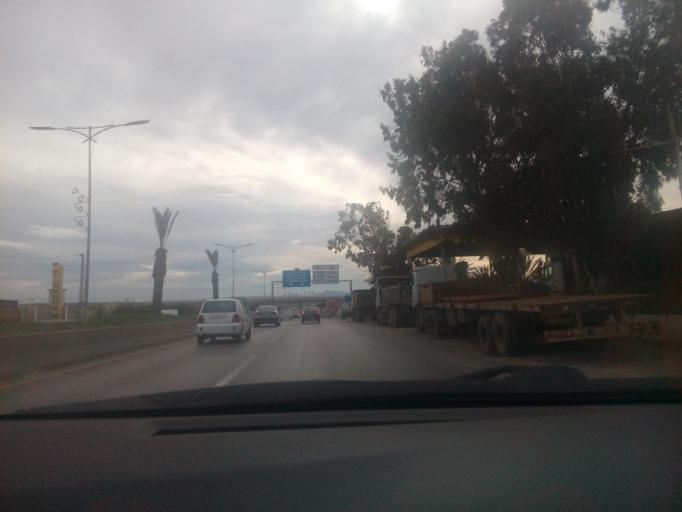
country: DZ
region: Oran
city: Es Senia
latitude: 35.6050
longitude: -0.5762
